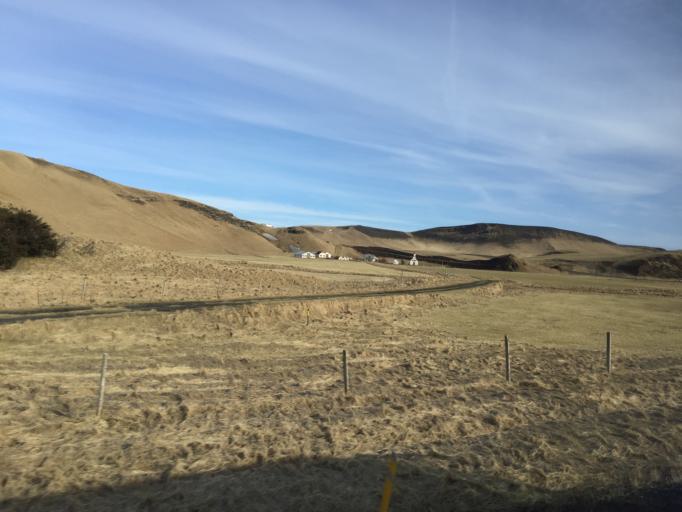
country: IS
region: South
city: Vestmannaeyjar
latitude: 63.4347
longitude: -19.1916
